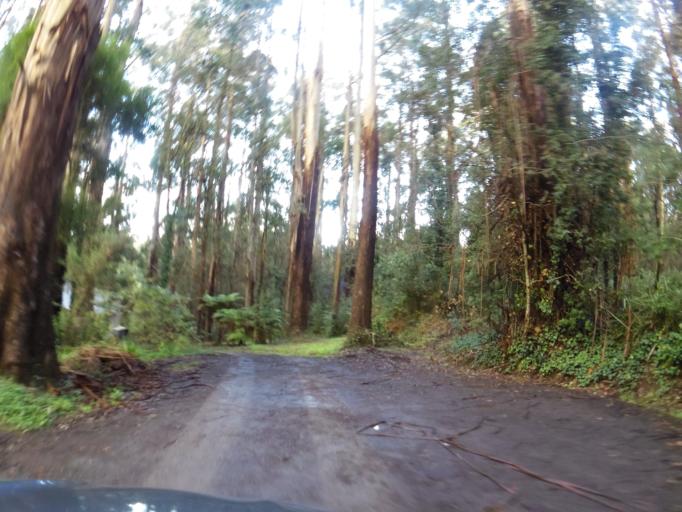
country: AU
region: Victoria
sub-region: Yarra Ranges
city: Kallista
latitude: -37.8760
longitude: 145.3634
